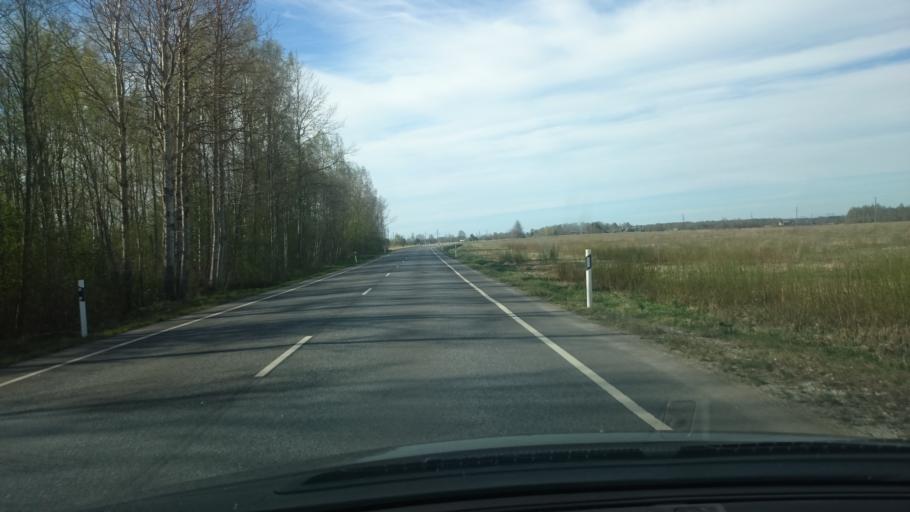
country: EE
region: Ida-Virumaa
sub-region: Johvi vald
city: Johvi
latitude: 59.2580
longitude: 27.5158
